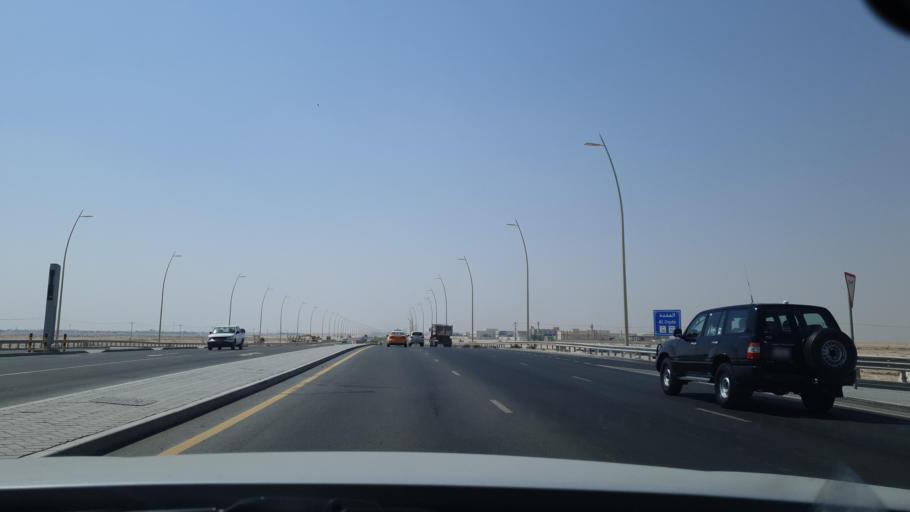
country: QA
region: Al Khawr
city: Al Khawr
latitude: 25.6658
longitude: 51.4755
